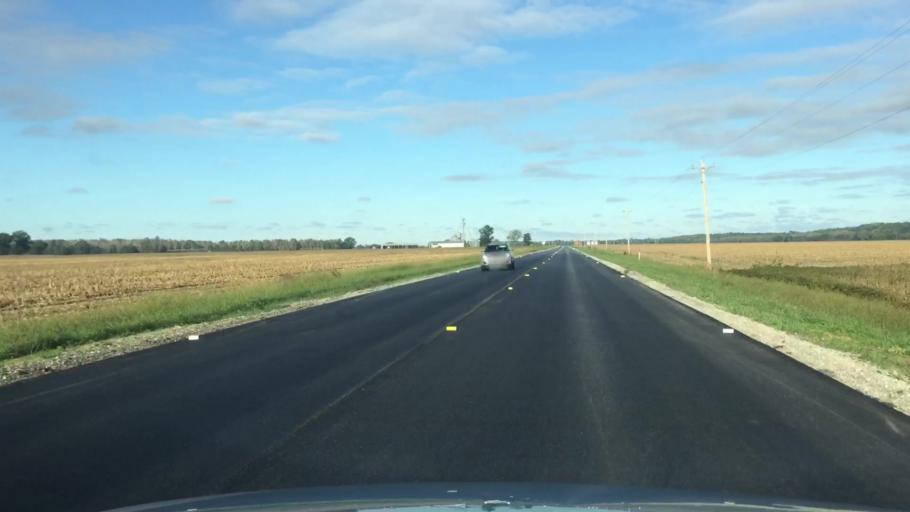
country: US
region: Missouri
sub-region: Howard County
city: New Franklin
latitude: 38.9948
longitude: -92.6577
